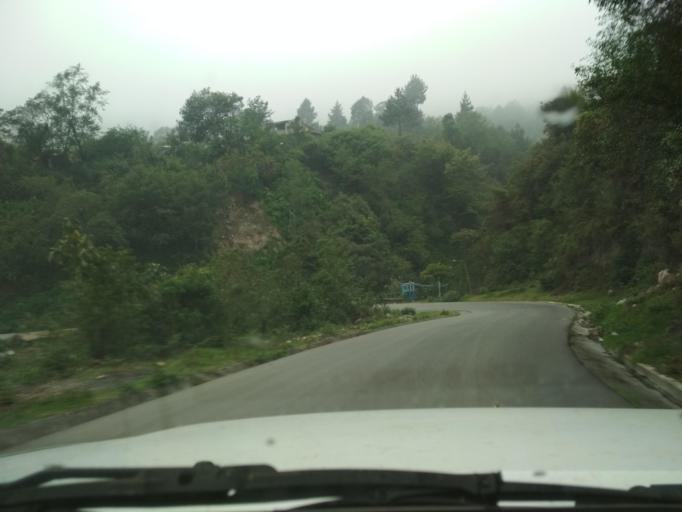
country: MX
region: Veracruz
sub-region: La Perla
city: Metlac Hernandez (Metlac Primero)
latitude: 18.9546
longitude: -97.1758
